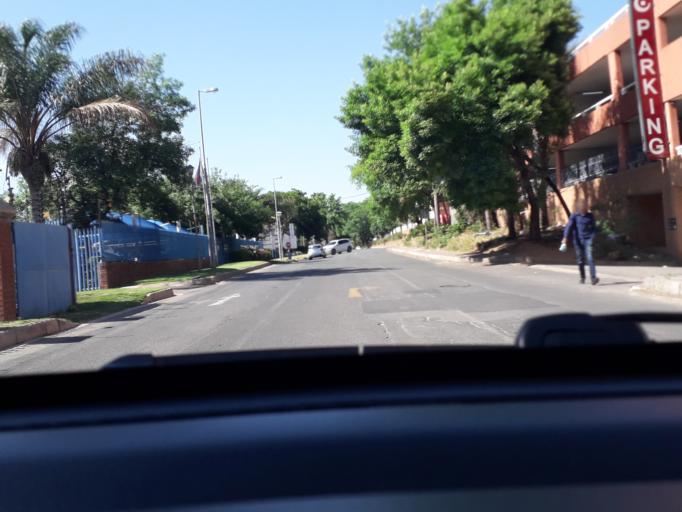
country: ZA
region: Gauteng
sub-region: City of Johannesburg Metropolitan Municipality
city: Midrand
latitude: -26.0566
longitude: 28.0617
